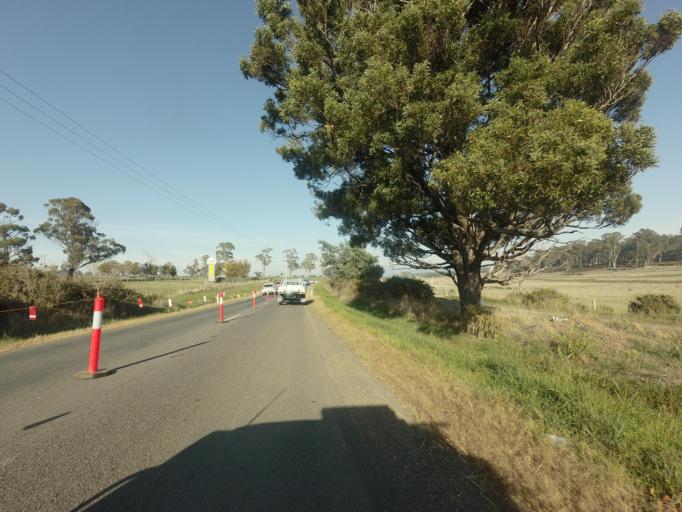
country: AU
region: Tasmania
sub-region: Northern Midlands
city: Longford
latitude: -41.5567
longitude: 146.9869
